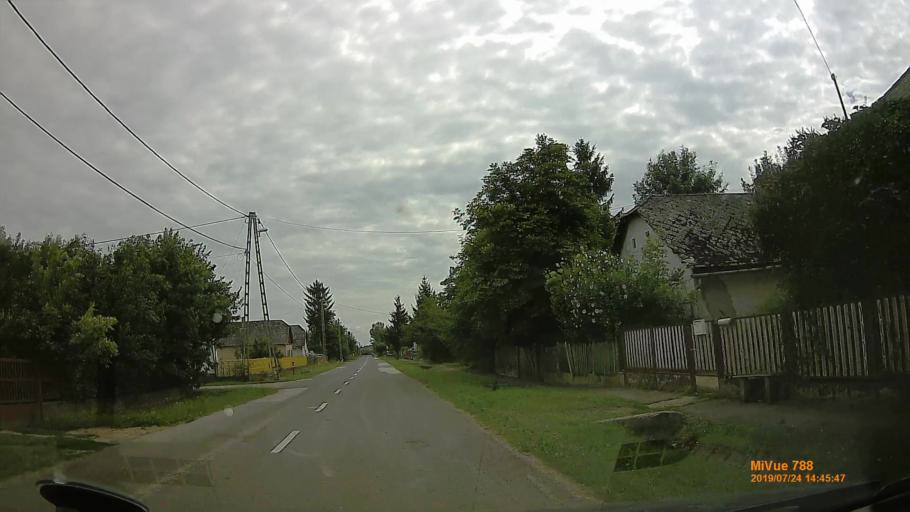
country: HU
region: Szabolcs-Szatmar-Bereg
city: Aranyosapati
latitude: 48.2906
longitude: 22.2824
